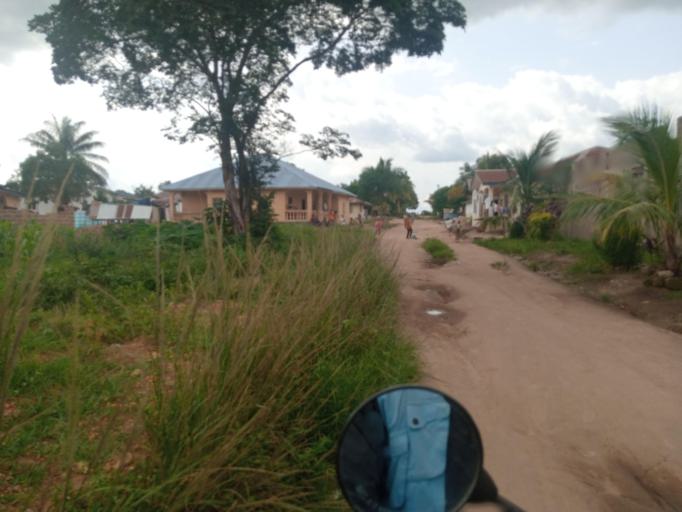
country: SL
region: Southern Province
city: Bo
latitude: 7.9831
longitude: -11.7406
